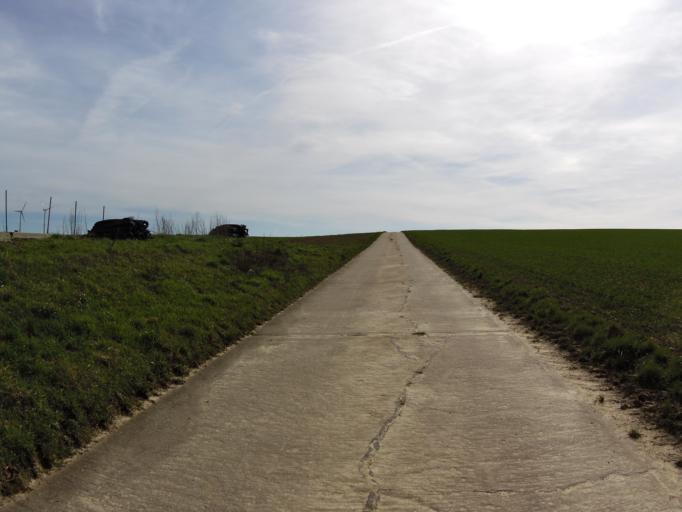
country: DE
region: Bavaria
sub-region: Regierungsbezirk Unterfranken
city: Biebelried
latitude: 49.7597
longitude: 10.0853
